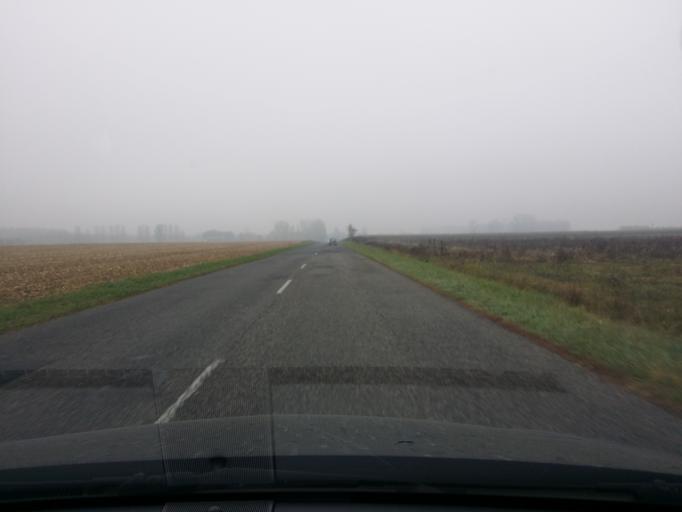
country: HU
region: Szabolcs-Szatmar-Bereg
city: Nyirbogdany
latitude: 48.0530
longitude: 21.8612
